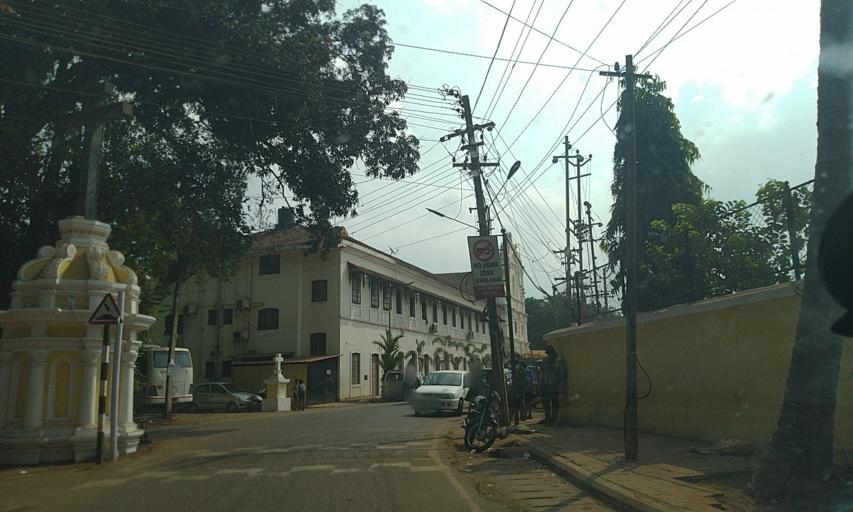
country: IN
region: Goa
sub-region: North Goa
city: Taleigao
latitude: 15.4759
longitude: 73.8441
